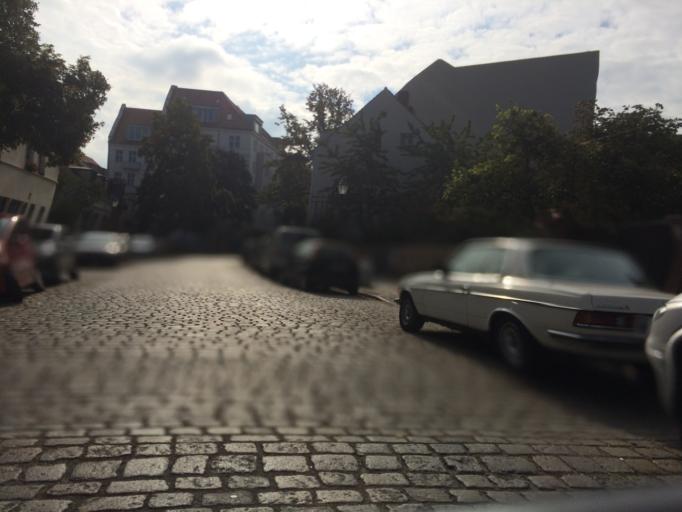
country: DE
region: Berlin
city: Berlin Treptow
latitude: 52.4755
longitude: 13.4439
